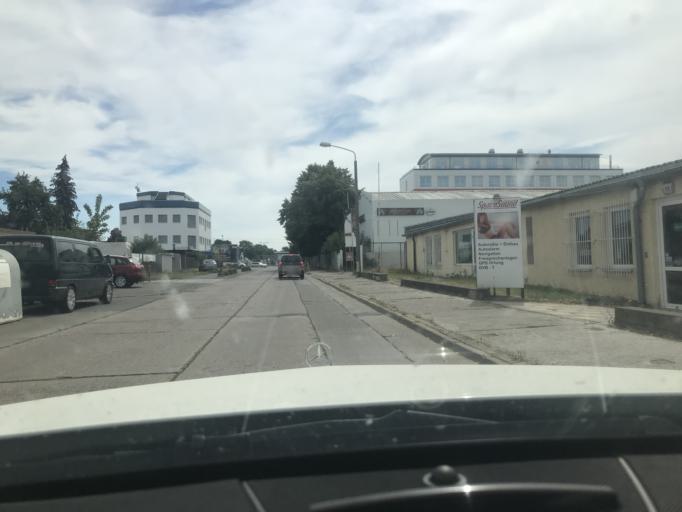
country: DE
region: Thuringia
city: Erfurt
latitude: 51.0101
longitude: 11.0311
